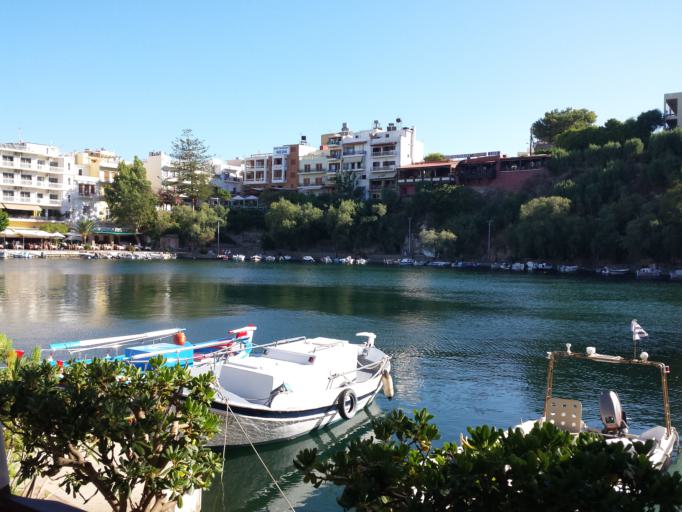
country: GR
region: Crete
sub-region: Nomos Lasithiou
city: Agios Nikolaos
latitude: 35.1912
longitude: 25.7173
